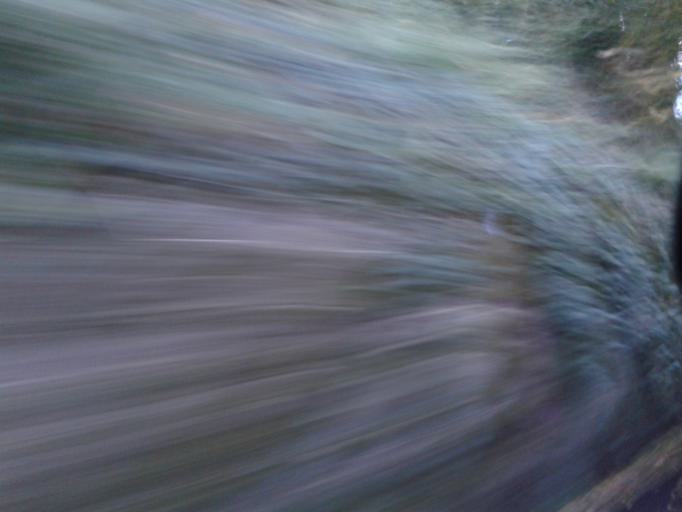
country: IE
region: Leinster
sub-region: An Mhi
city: Slane
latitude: 53.6886
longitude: -6.4956
